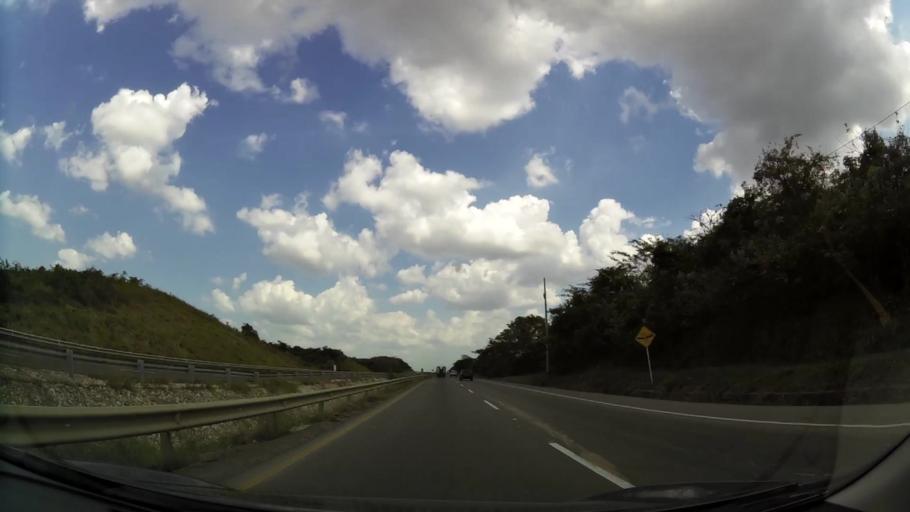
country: CO
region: Bolivar
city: Cartagena
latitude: 10.3609
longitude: -75.4662
